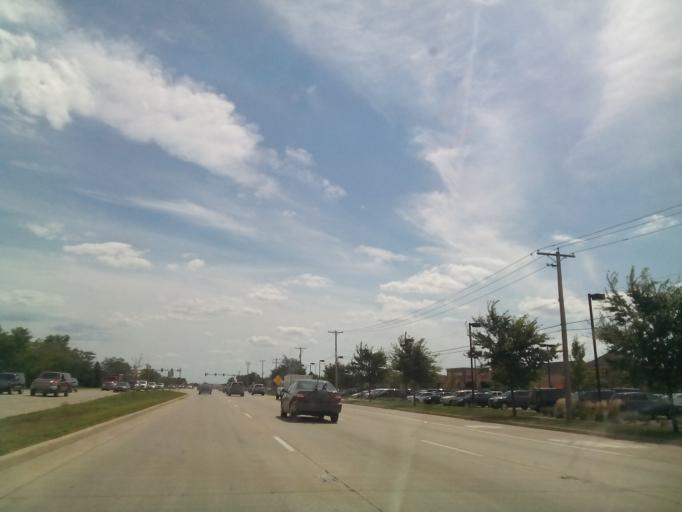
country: US
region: Illinois
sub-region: Will County
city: Plainfield
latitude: 41.7122
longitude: -88.2060
